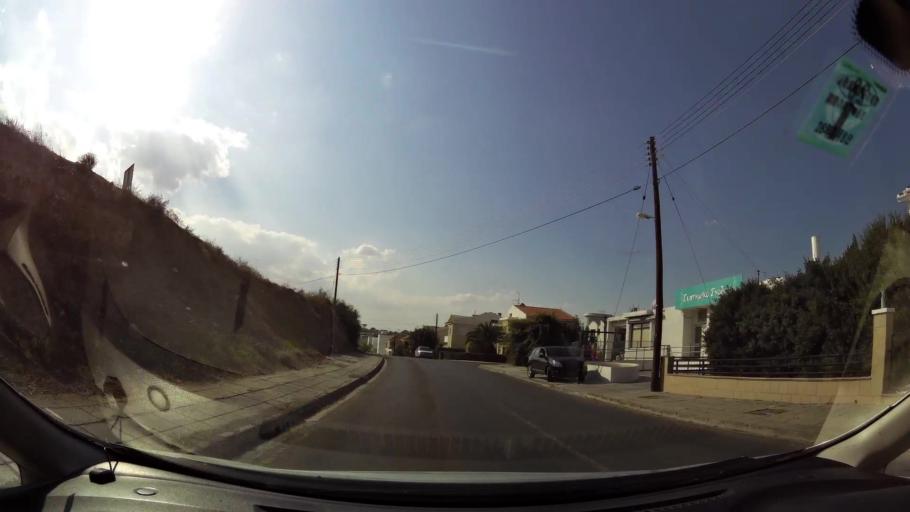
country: CY
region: Lefkosia
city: Nicosia
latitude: 35.1519
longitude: 33.3072
